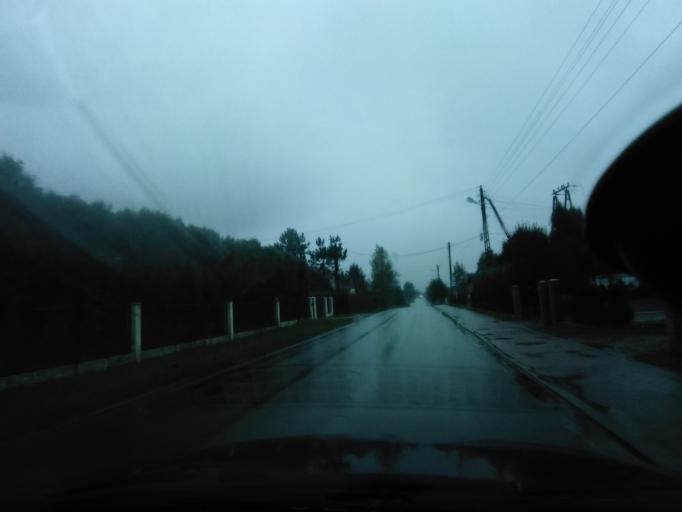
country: PL
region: Subcarpathian Voivodeship
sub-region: Powiat krosnienski
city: Miejsce Piastowe
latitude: 49.6548
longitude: 21.8064
